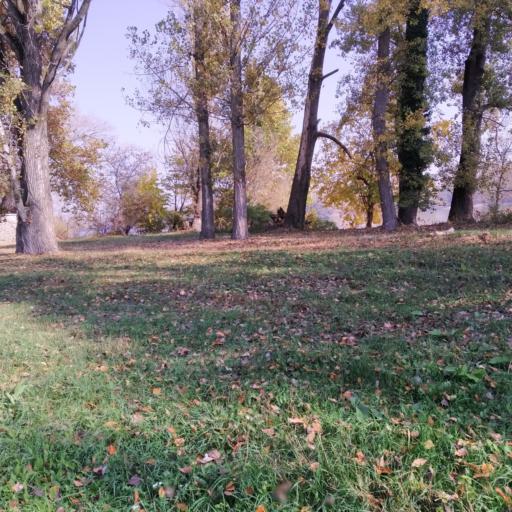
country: HU
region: Budapest
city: Budapest IV. keruelet
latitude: 47.5922
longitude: 19.0738
